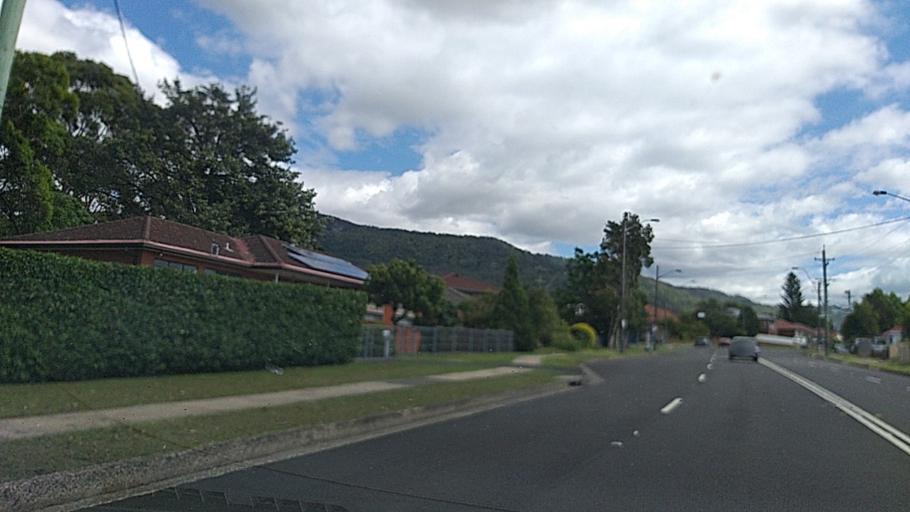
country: AU
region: New South Wales
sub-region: Wollongong
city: Corrimal
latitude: -34.3792
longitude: 150.8967
